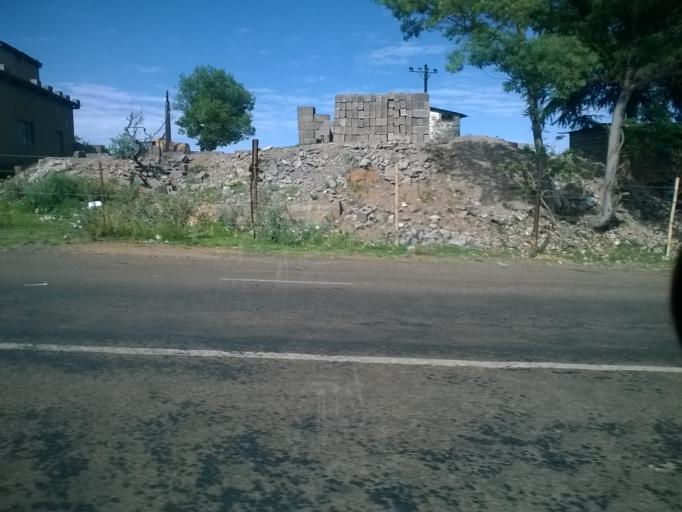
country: LS
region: Berea
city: Teyateyaneng
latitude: -29.1016
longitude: 27.9596
